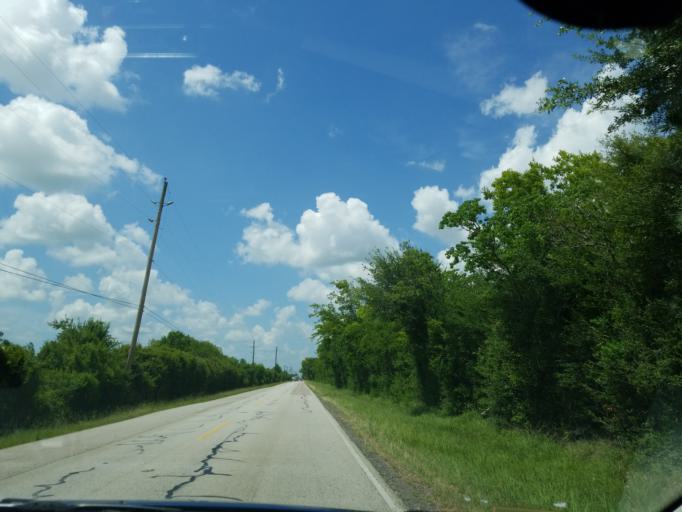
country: US
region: Texas
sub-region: Harris County
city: Katy
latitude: 29.8690
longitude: -95.8072
